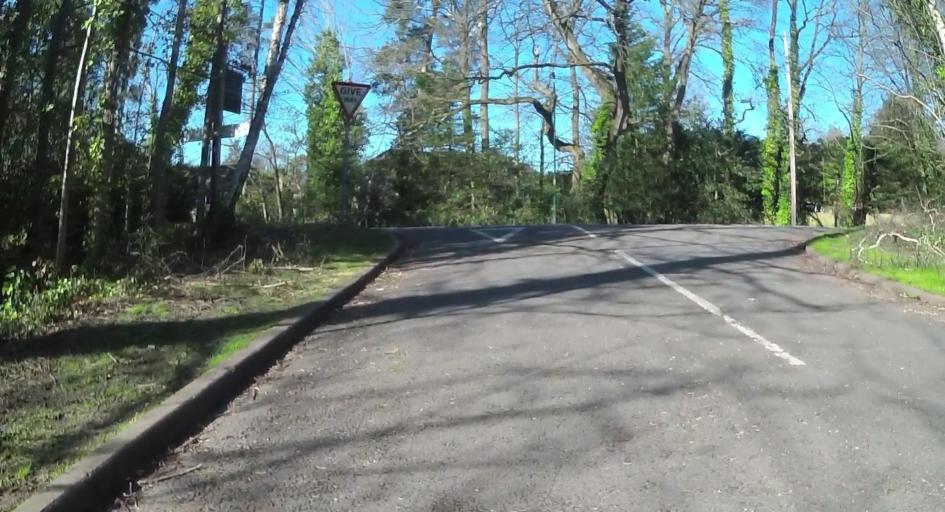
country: GB
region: England
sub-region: Royal Borough of Windsor and Maidenhead
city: Ascot
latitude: 51.3963
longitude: -0.6627
